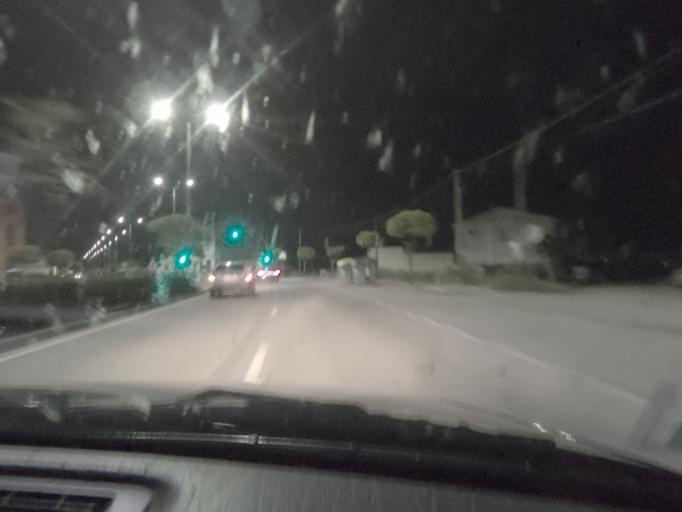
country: ES
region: Extremadura
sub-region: Provincia de Caceres
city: Moraleja
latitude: 40.0725
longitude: -6.6594
